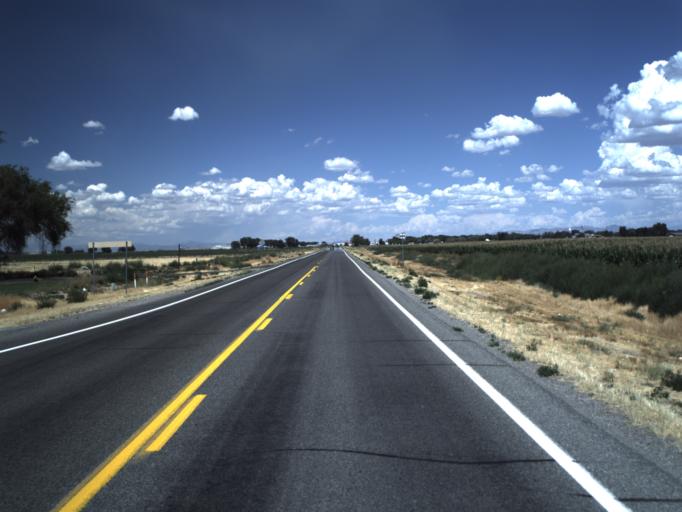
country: US
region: Utah
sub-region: Millard County
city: Delta
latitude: 39.3388
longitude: -112.6057
